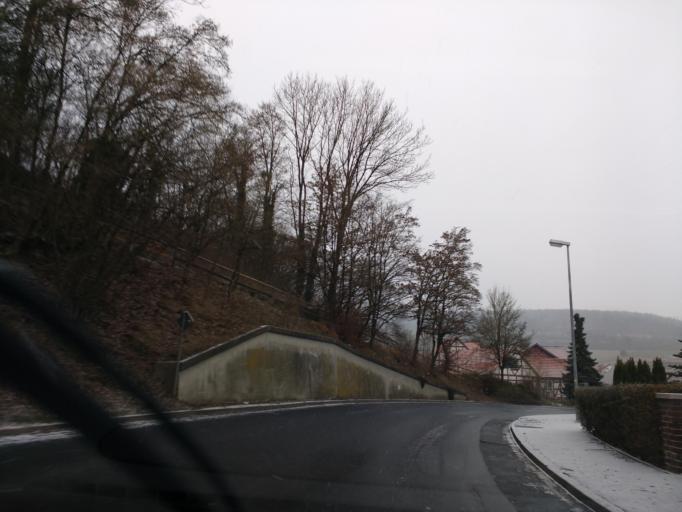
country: DE
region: Hesse
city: Spangenberg
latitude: 51.1155
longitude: 9.6594
